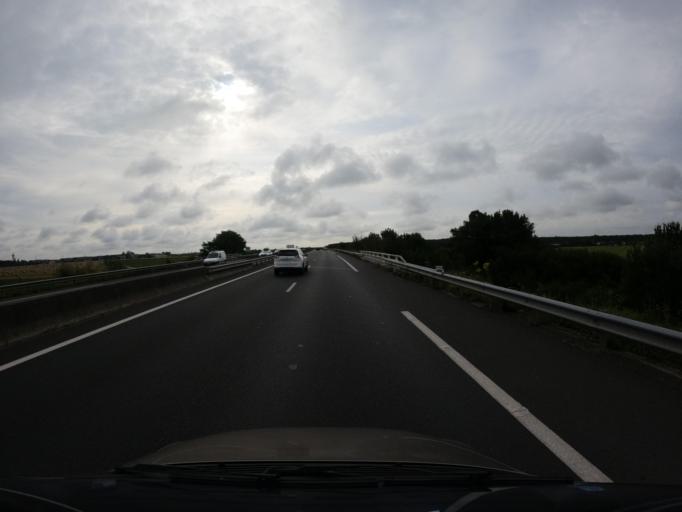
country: FR
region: Centre
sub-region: Departement d'Indre-et-Loire
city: Villandry
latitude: 47.3043
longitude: 0.5230
